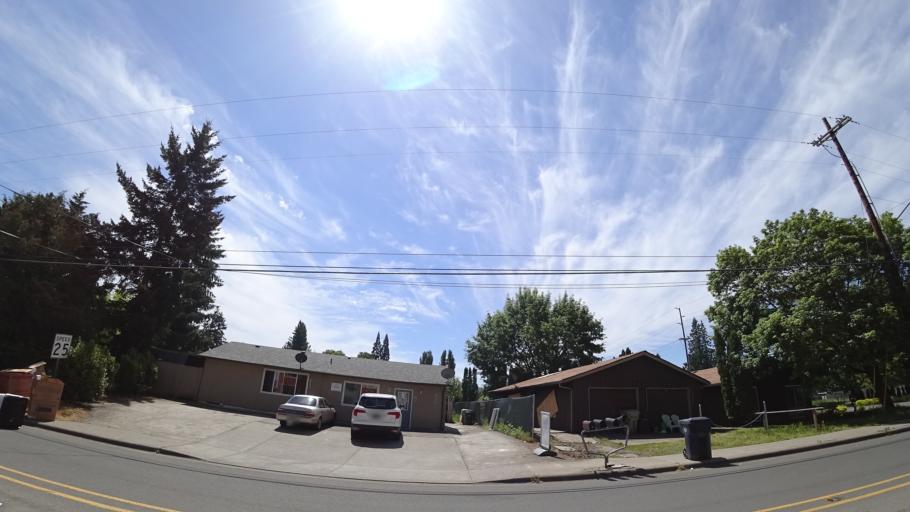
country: US
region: Oregon
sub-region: Washington County
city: Aloha
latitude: 45.4905
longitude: -122.8515
